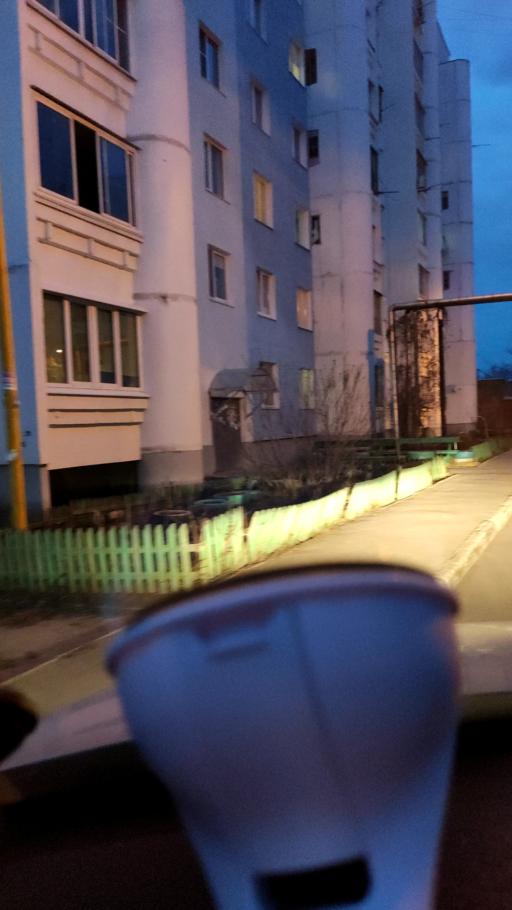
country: RU
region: Samara
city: Volzhskiy
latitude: 53.3529
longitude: 50.2107
